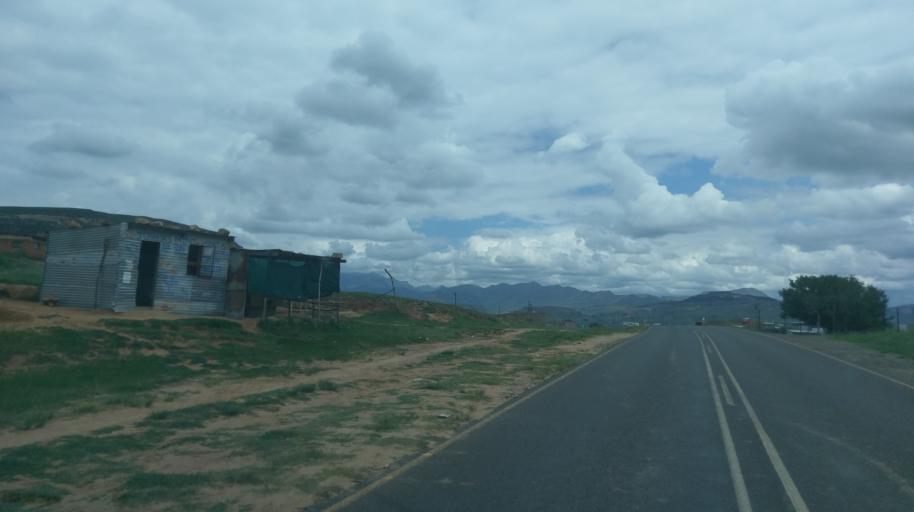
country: LS
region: Leribe
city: Leribe
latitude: -28.9479
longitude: 28.1692
